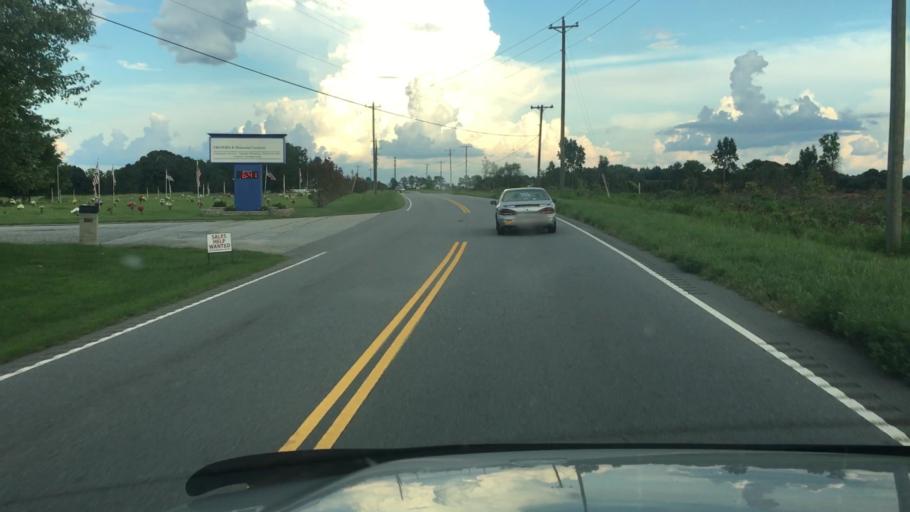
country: US
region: South Carolina
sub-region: Cherokee County
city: Gaffney
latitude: 35.1053
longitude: -81.6955
